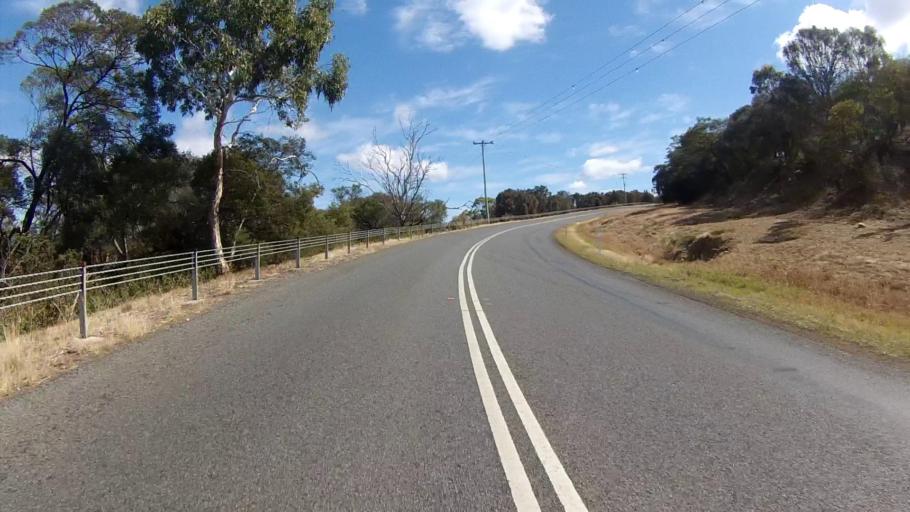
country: AU
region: Tasmania
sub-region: Brighton
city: Bridgewater
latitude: -42.7096
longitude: 147.2692
